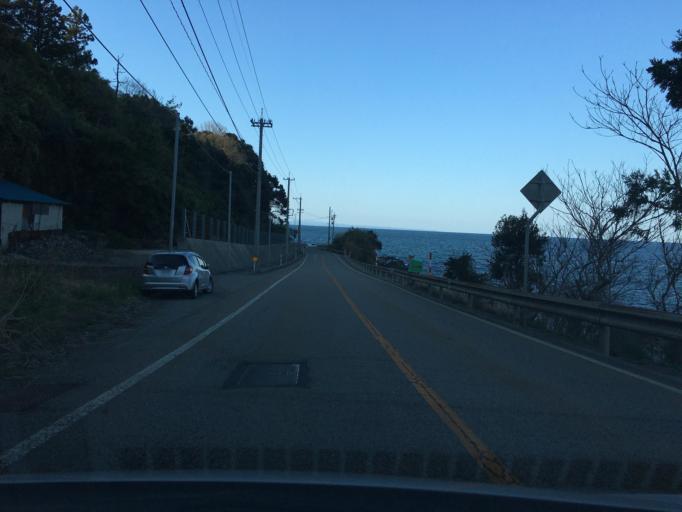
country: JP
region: Ishikawa
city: Nanao
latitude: 36.9927
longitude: 137.0529
